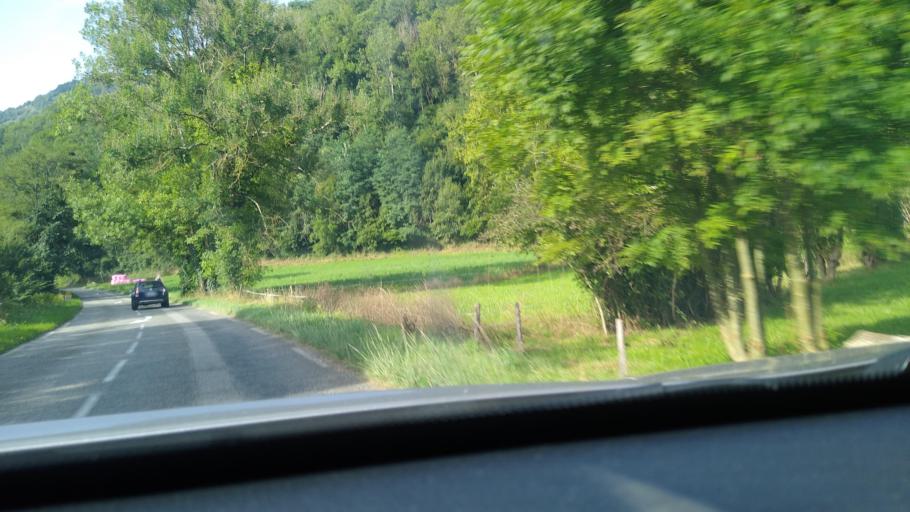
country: FR
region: Midi-Pyrenees
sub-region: Departement de l'Ariege
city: Saint-Girons
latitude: 42.9488
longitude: 1.1704
